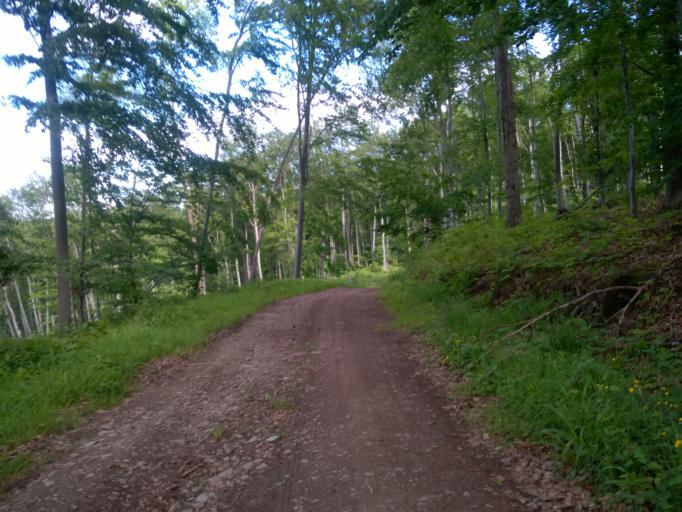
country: SK
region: Kosicky
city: Secovce
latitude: 48.7231
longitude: 21.5296
